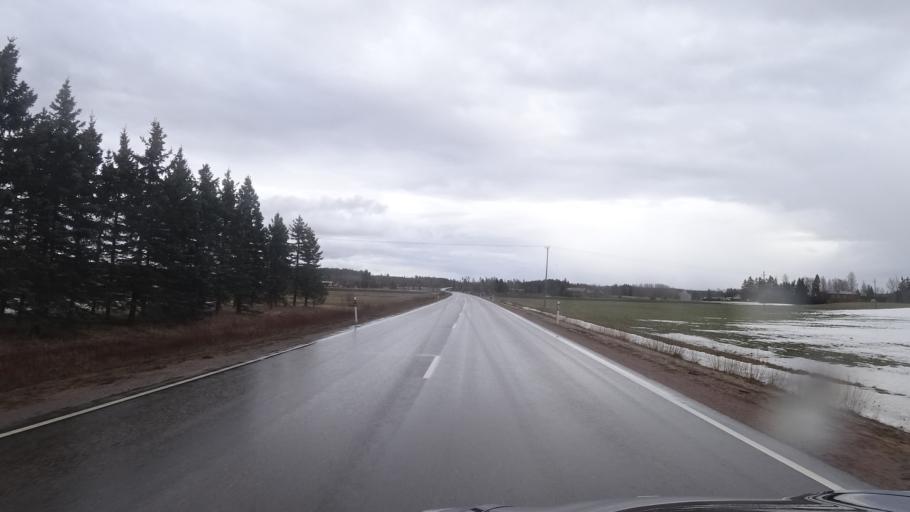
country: FI
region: Kymenlaakso
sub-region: Kouvola
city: Elimaeki
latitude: 60.7128
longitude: 26.4484
